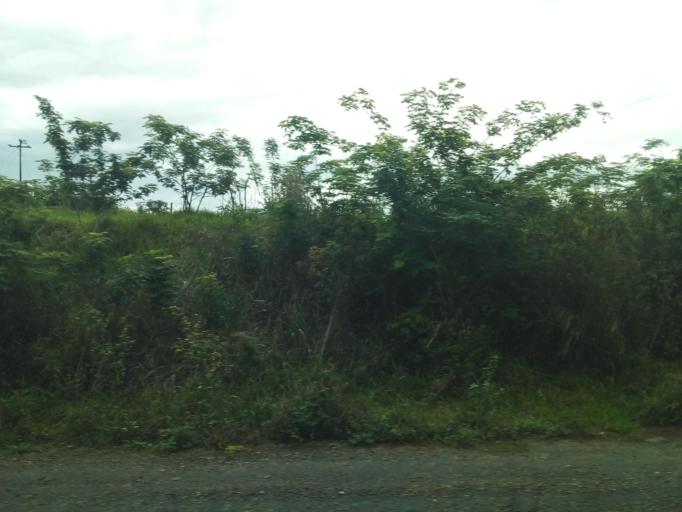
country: BR
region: Minas Gerais
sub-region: Governador Valadares
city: Governador Valadares
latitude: -19.0889
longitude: -42.1632
